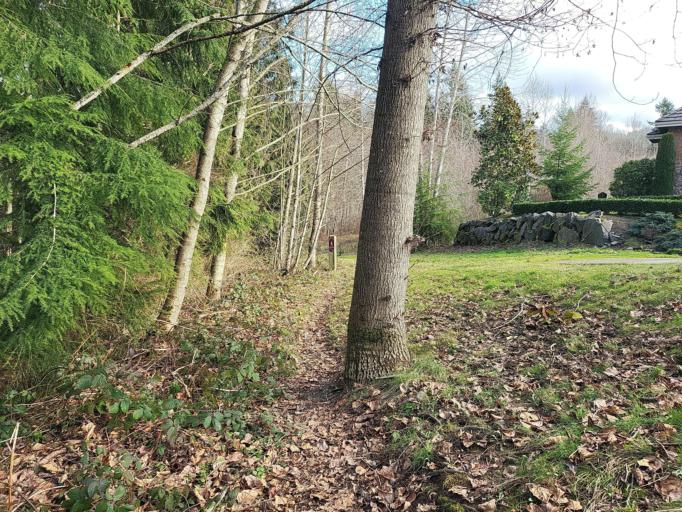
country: US
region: Washington
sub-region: King County
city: Newcastle
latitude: 47.5326
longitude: -122.1313
